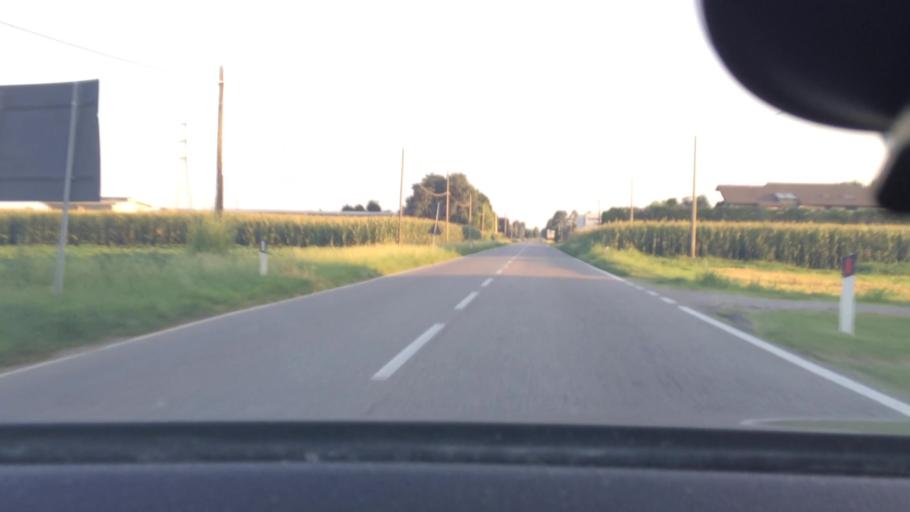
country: IT
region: Lombardy
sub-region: Provincia di Como
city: Turate
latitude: 45.6702
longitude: 9.0020
